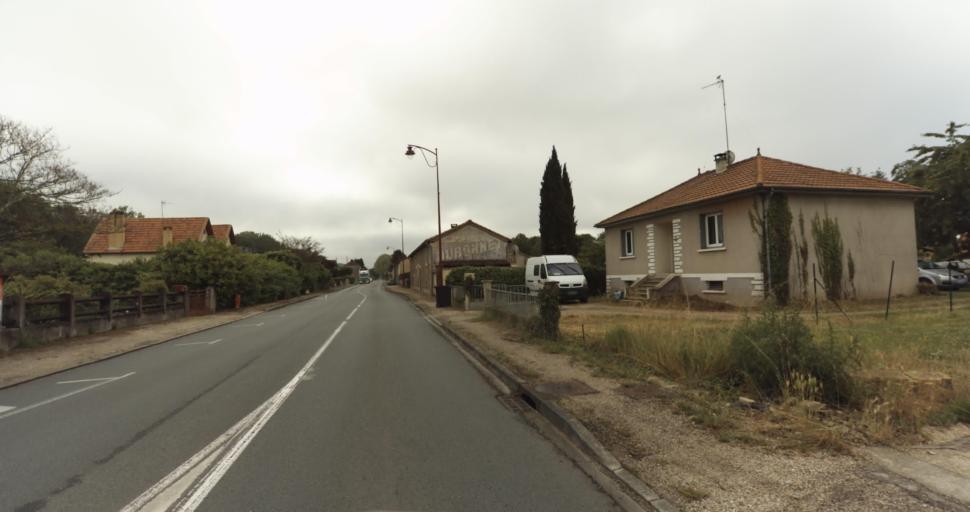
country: FR
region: Aquitaine
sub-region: Departement de la Dordogne
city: Mouleydier
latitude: 44.8483
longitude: 0.6288
